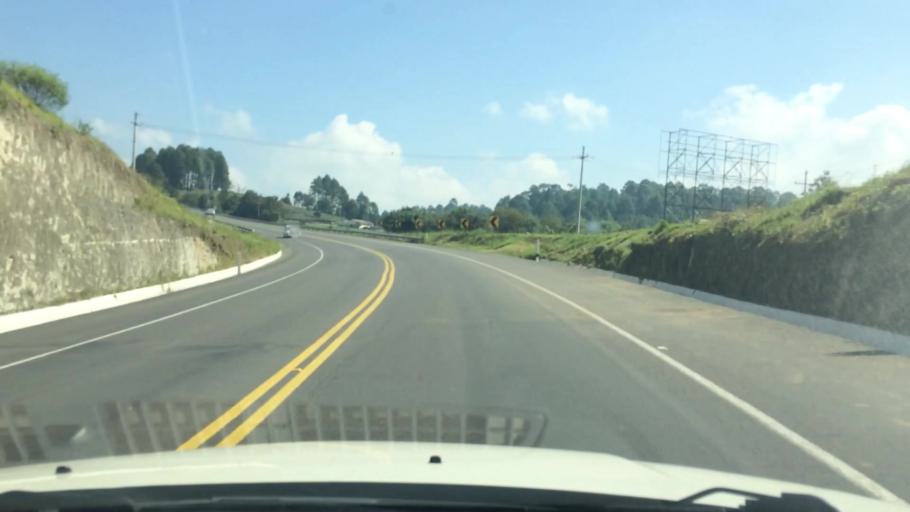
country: MX
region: Mexico
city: Amanalco de Becerra
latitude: 19.2975
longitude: -100.0129
